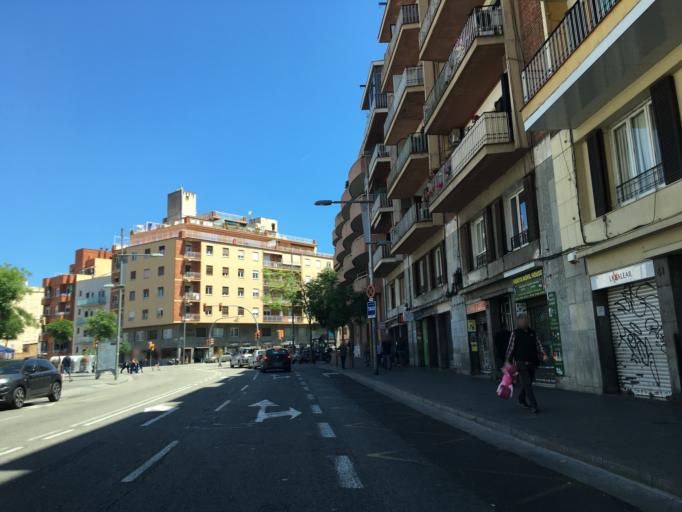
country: ES
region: Catalonia
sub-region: Provincia de Barcelona
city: Horta-Guinardo
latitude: 41.4296
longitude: 2.1612
